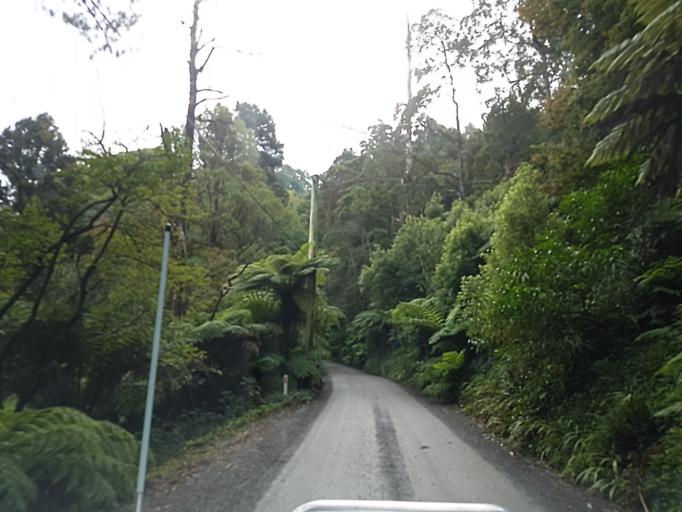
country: AU
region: Victoria
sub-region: Yarra Ranges
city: Monbulk
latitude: -37.8801
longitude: 145.3847
